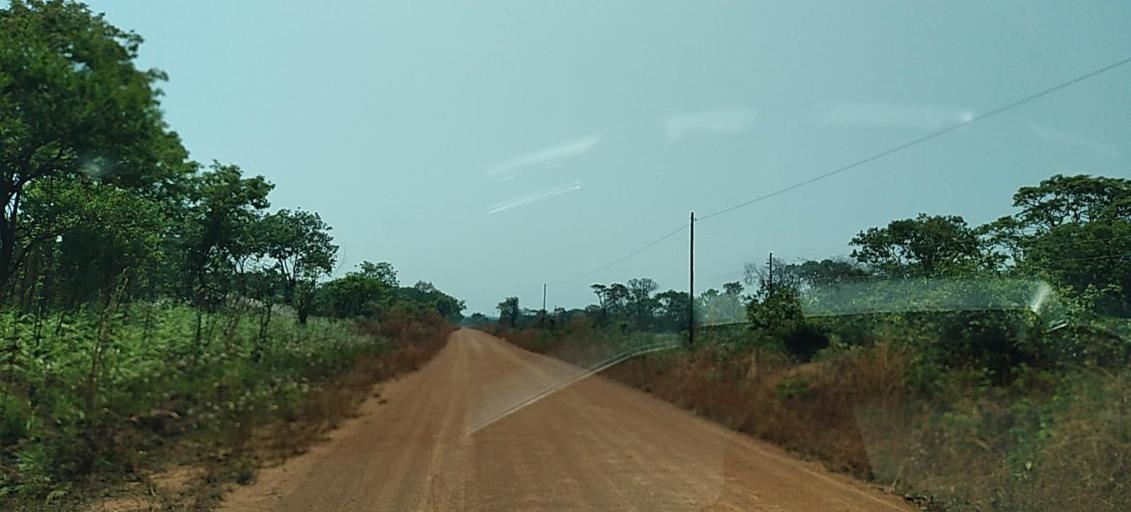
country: ZM
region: North-Western
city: Kansanshi
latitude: -11.9956
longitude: 26.6518
